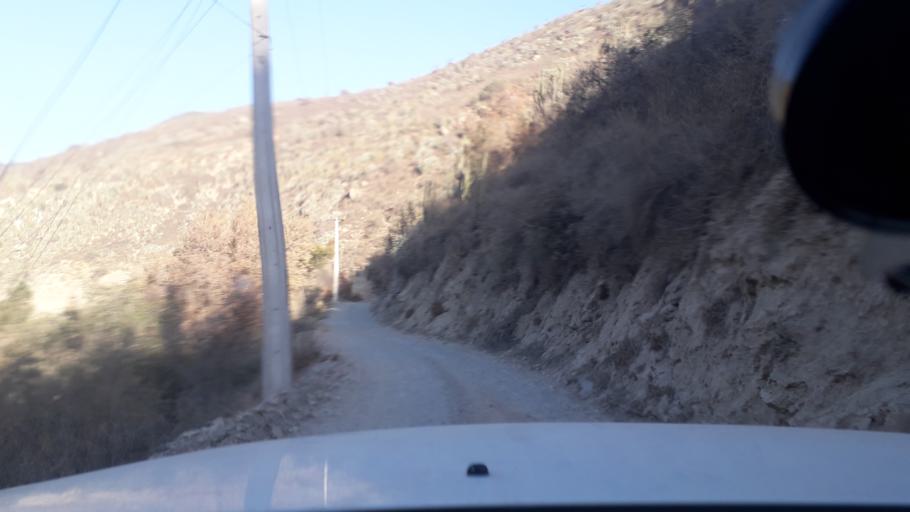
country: CL
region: Valparaiso
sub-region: Provincia de Marga Marga
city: Limache
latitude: -33.0515
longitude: -71.0832
